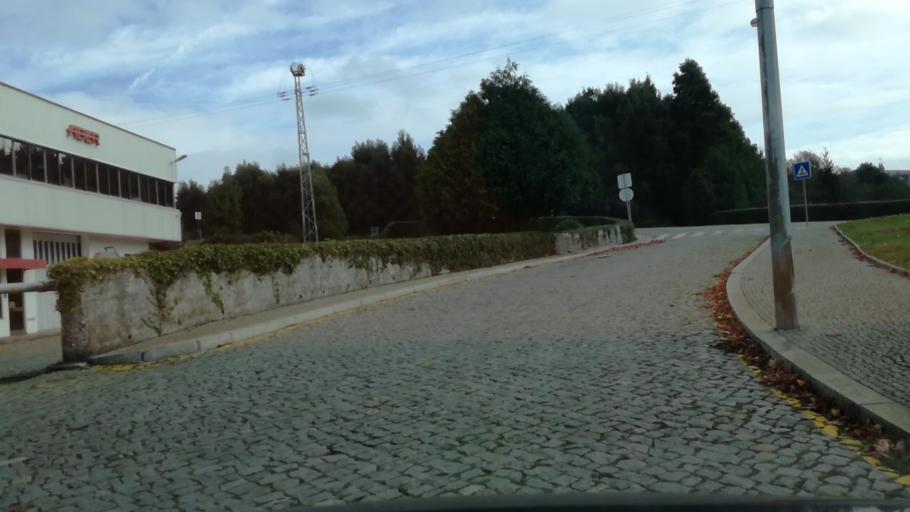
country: PT
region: Porto
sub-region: Maia
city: Gemunde
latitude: 41.2538
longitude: -8.6687
